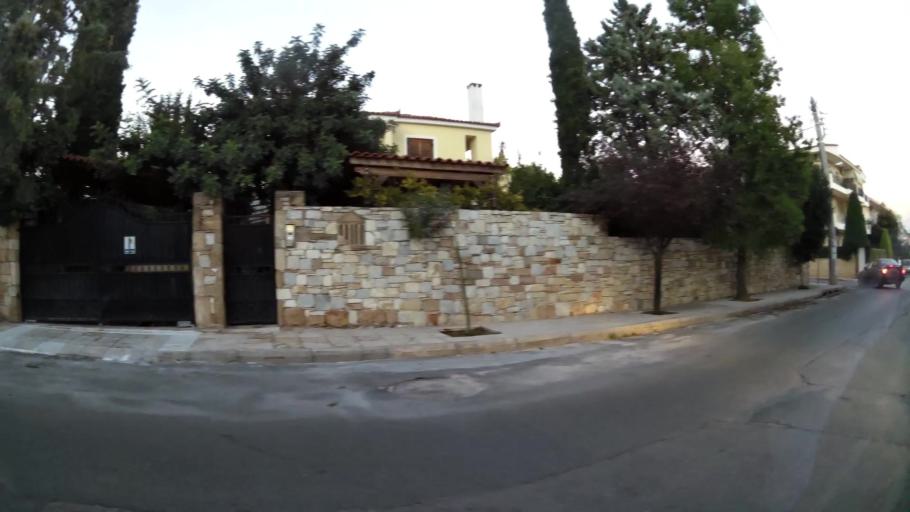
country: GR
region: Attica
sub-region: Nomarchia Anatolikis Attikis
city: Paiania
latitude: 37.9512
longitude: 23.8558
